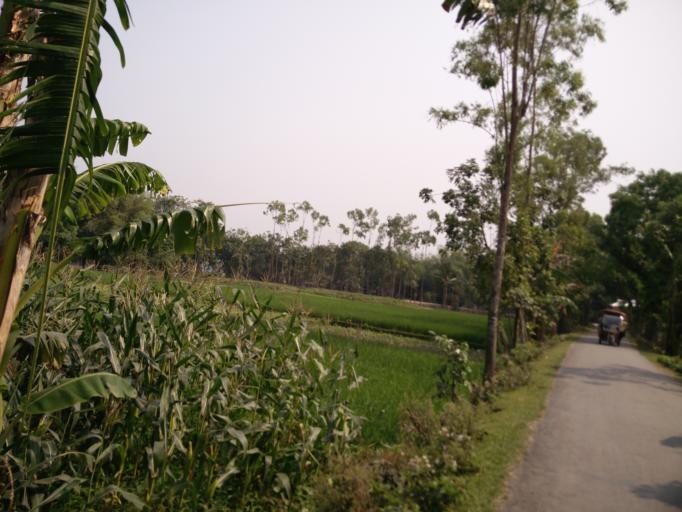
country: BD
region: Dhaka
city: Muktagacha
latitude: 24.9204
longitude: 90.2387
